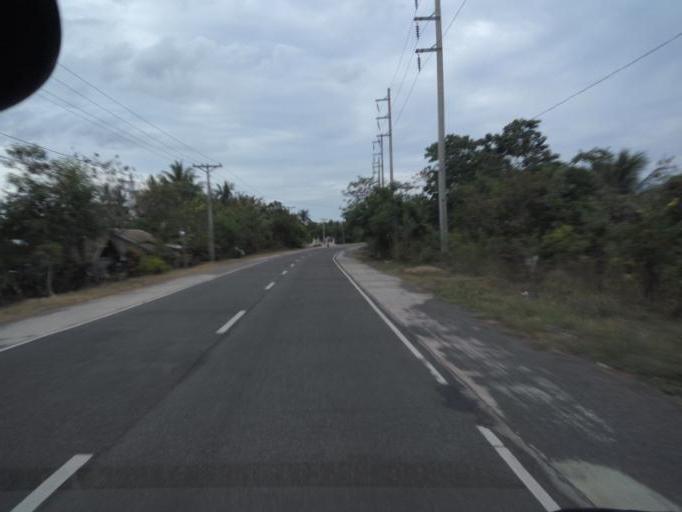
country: PH
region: Cagayan Valley
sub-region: Province of Cagayan
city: Casambalangan
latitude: 18.3998
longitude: 122.1254
